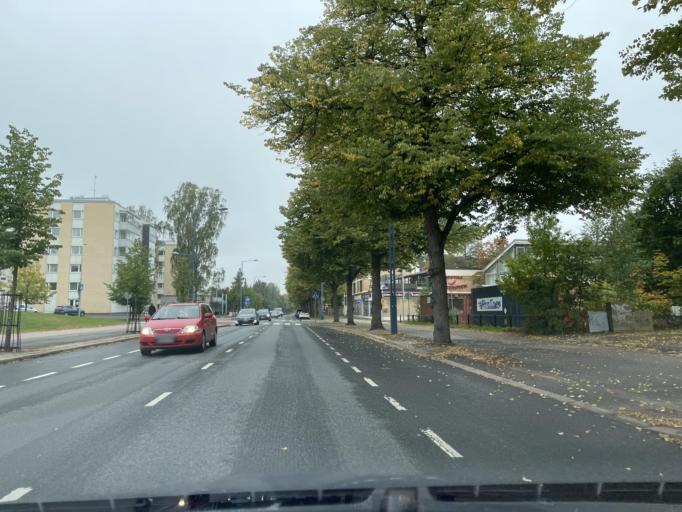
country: FI
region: Uusimaa
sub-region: Helsinki
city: Hyvinge
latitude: 60.6266
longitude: 24.8543
